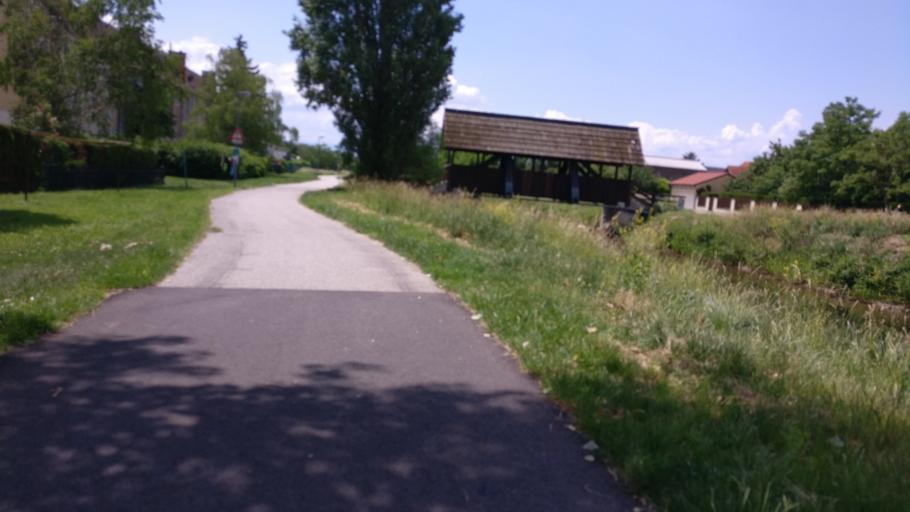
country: AT
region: Lower Austria
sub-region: Politischer Bezirk Wiener Neustadt
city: Lichtenworth
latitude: 47.8332
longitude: 16.2633
